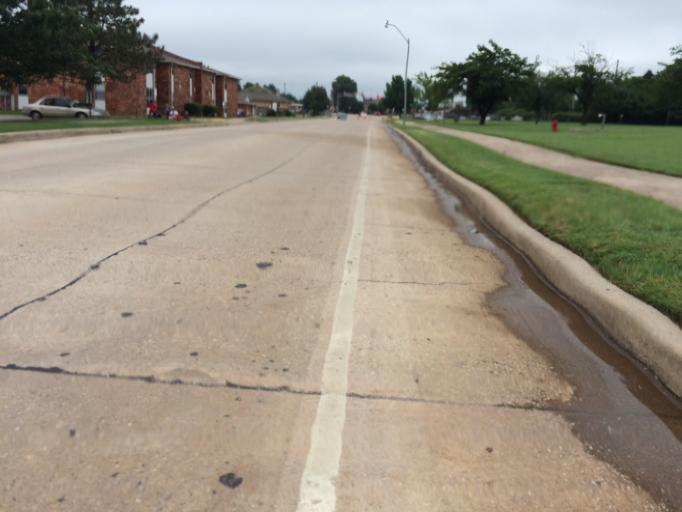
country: US
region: Oklahoma
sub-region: Cleveland County
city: Hall Park
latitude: 35.2162
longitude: -97.4118
